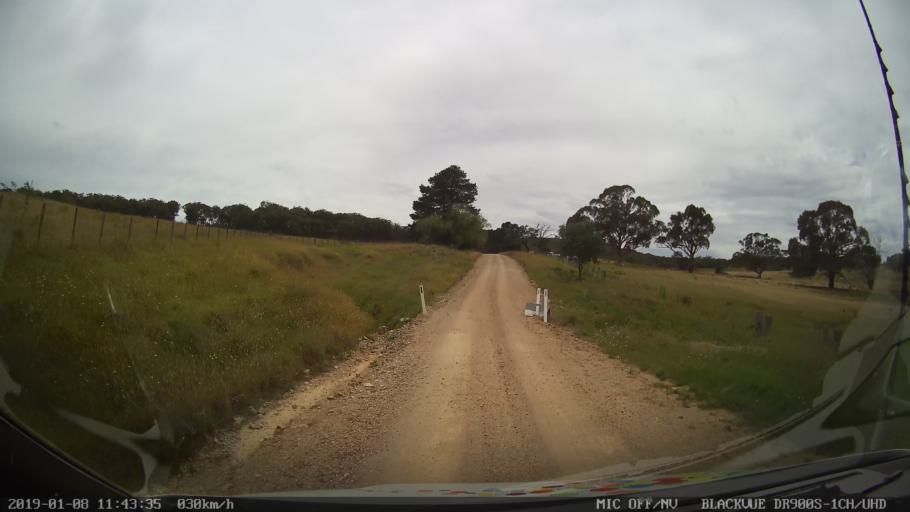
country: AU
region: New South Wales
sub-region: Armidale Dumaresq
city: Armidale
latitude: -30.3810
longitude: 151.5827
